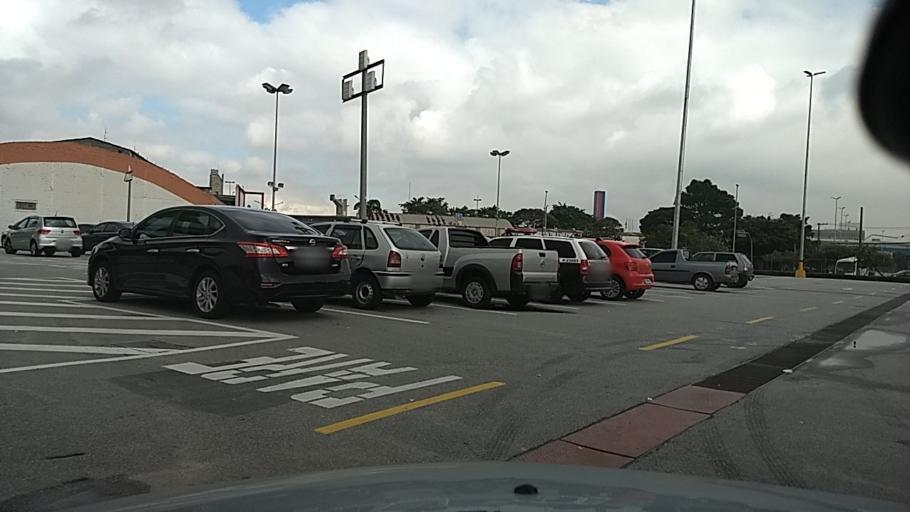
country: BR
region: Sao Paulo
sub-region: Sao Paulo
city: Sao Paulo
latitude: -23.5172
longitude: -46.6155
